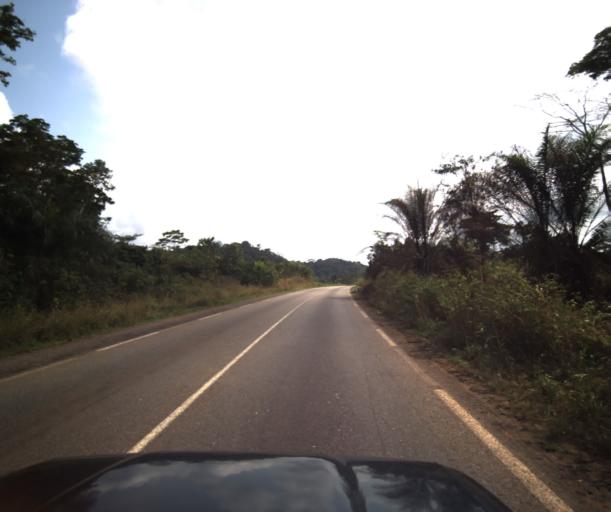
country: CM
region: Littoral
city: Edea
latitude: 3.7898
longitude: 10.2062
